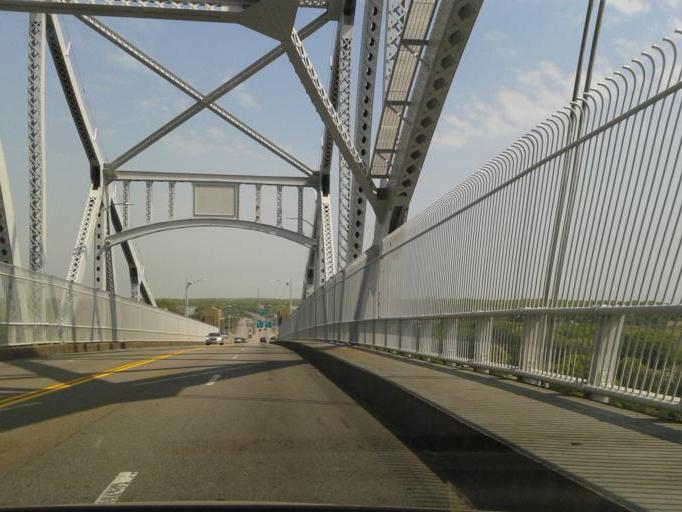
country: US
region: Massachusetts
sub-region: Barnstable County
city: Sagamore
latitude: 41.7766
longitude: -70.5434
